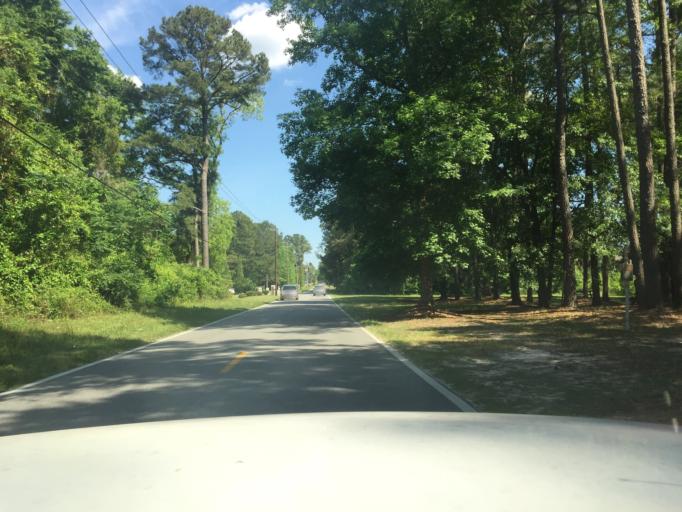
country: US
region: Georgia
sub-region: Chatham County
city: Georgetown
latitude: 32.0012
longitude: -81.2782
